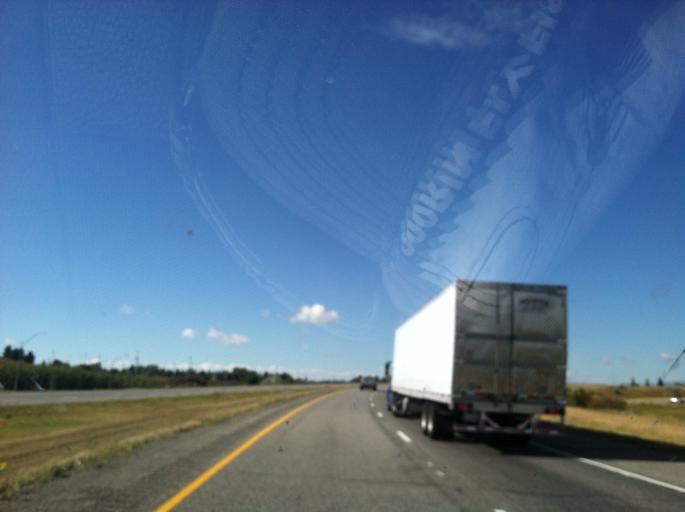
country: US
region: Montana
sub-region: Gallatin County
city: Bozeman
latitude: 45.6739
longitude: -111.0087
